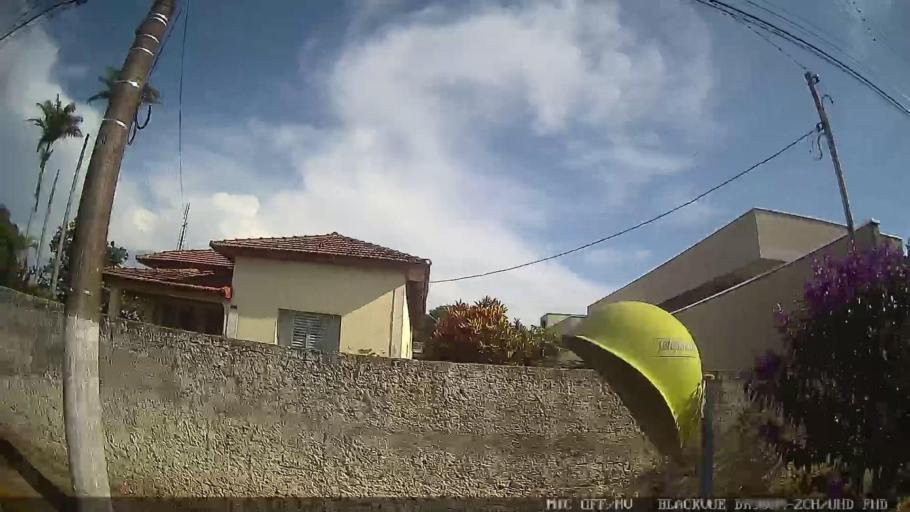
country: BR
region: Sao Paulo
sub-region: Laranjal Paulista
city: Laranjal Paulista
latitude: -23.0850
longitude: -47.7913
